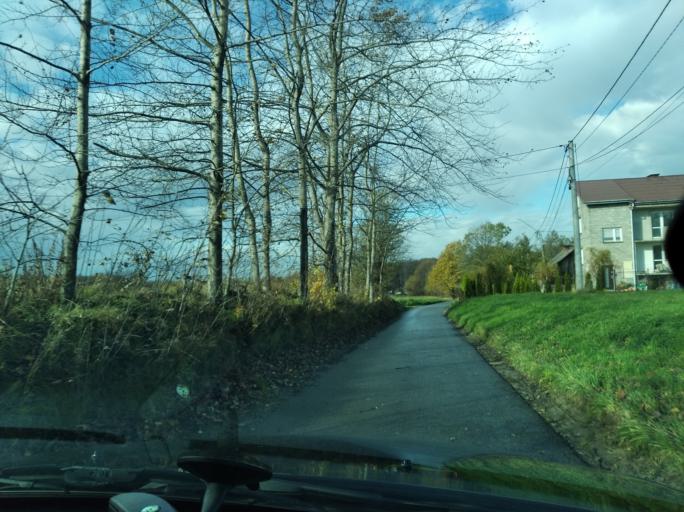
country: PL
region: Subcarpathian Voivodeship
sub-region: Powiat debicki
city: Debica
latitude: 50.0288
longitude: 21.4619
